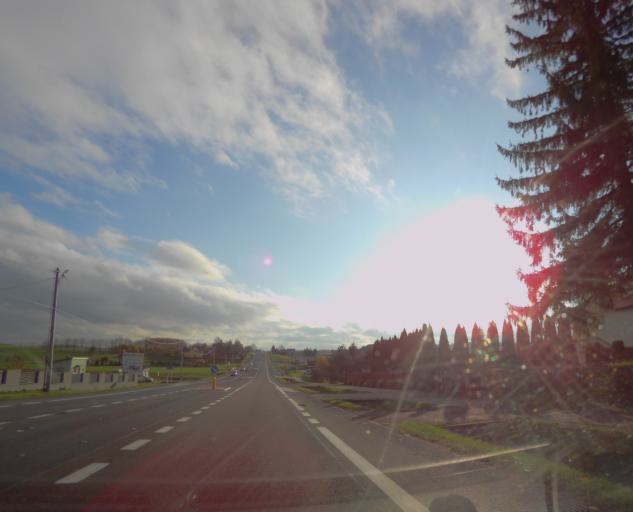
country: PL
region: Subcarpathian Voivodeship
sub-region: Powiat przemyski
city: Orly
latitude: 49.8575
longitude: 22.8064
